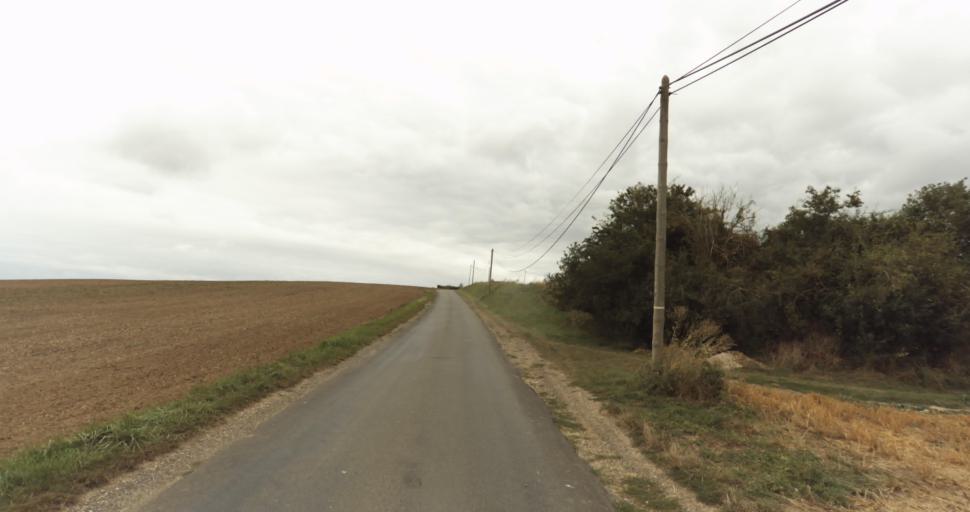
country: FR
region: Haute-Normandie
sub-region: Departement de l'Eure
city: Menilles
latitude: 49.0203
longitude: 1.3014
